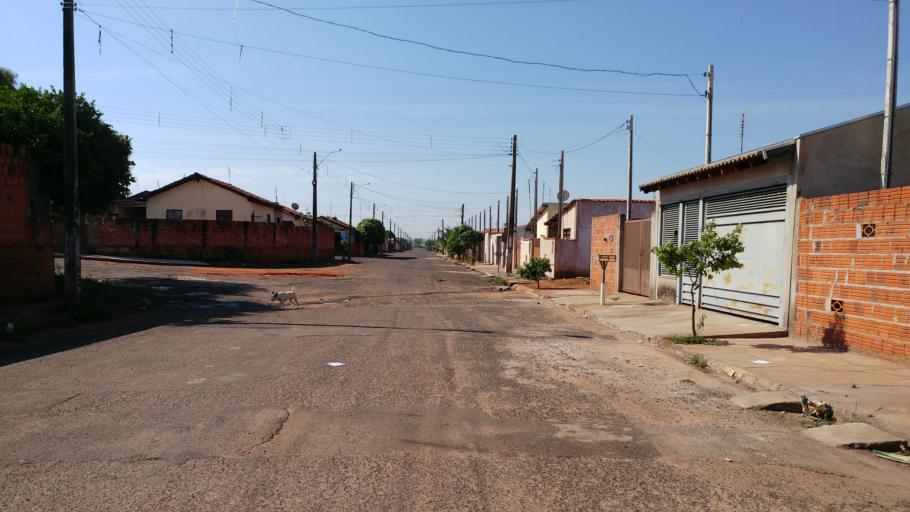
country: BR
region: Sao Paulo
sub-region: Paraguacu Paulista
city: Paraguacu Paulista
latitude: -22.4106
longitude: -50.5634
